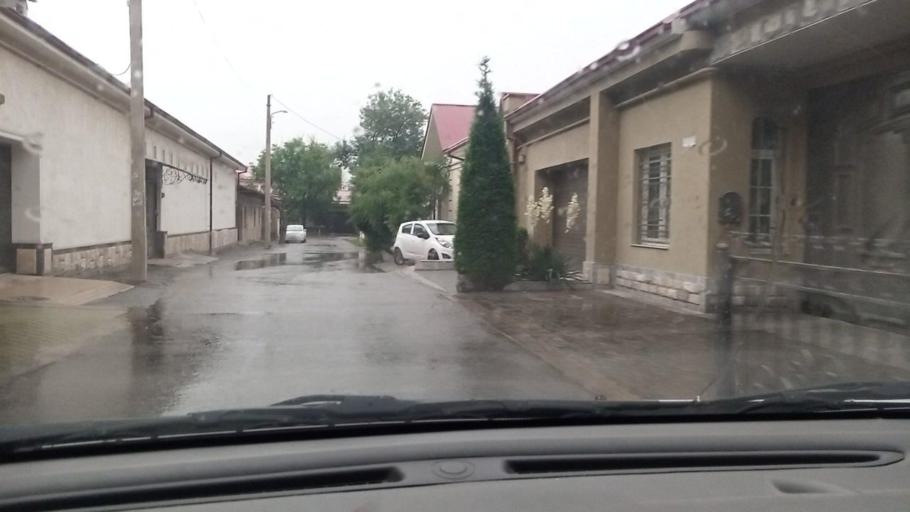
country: UZ
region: Toshkent
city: Salor
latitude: 41.3334
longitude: 69.3573
